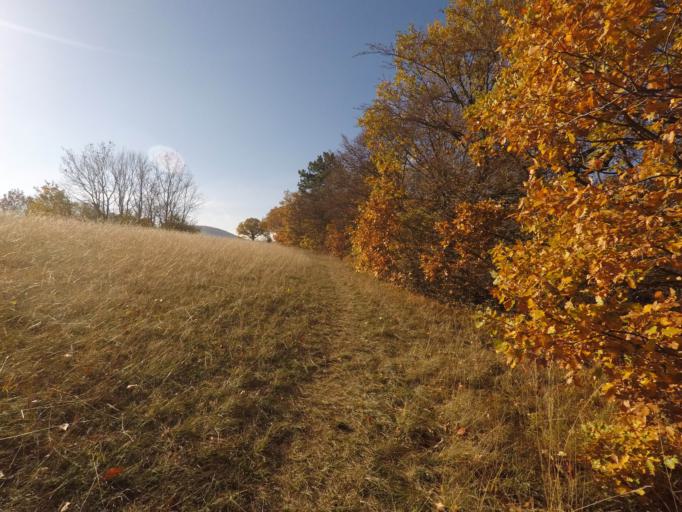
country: DE
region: Baden-Wuerttemberg
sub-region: Tuebingen Region
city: Pfullingen
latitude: 48.4470
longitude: 9.2220
